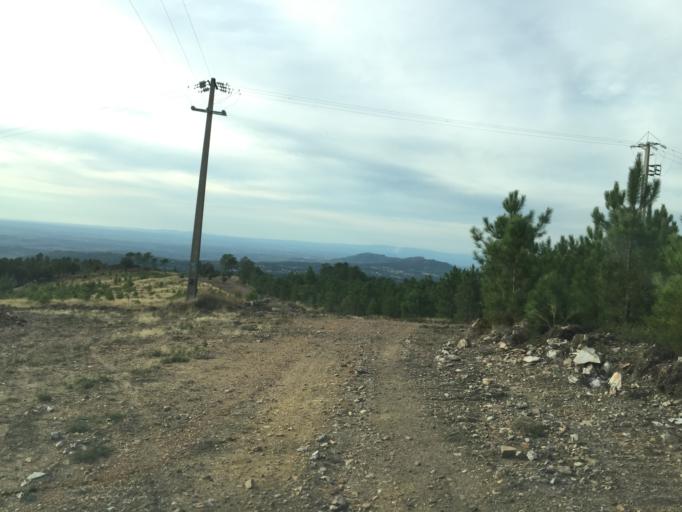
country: PT
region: Portalegre
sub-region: Portalegre
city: Reguengo
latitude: 39.3134
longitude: -7.3612
